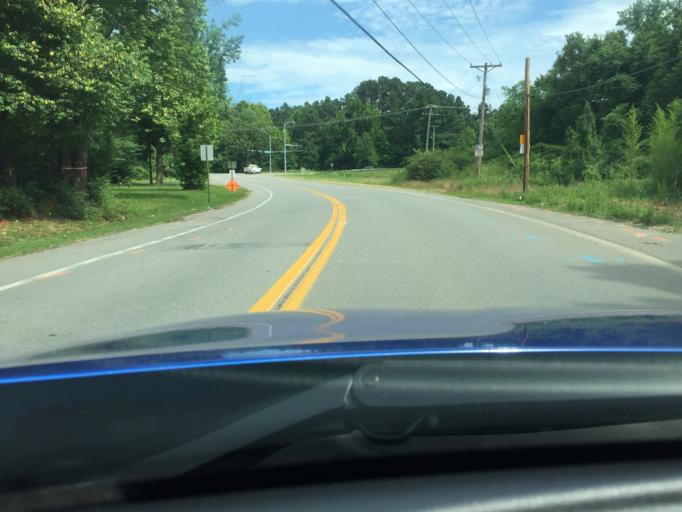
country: US
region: Arkansas
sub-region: Pulaski County
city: Maumelle
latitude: 34.8034
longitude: -92.4341
